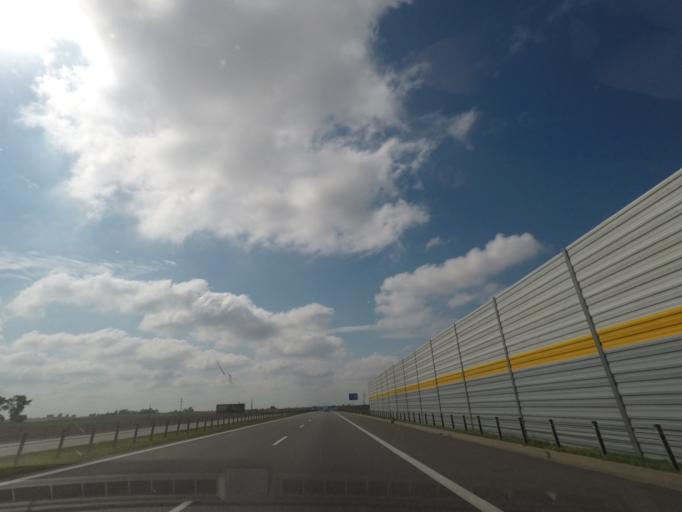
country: PL
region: Kujawsko-Pomorskie
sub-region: Powiat chelminski
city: Lisewo
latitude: 53.3031
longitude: 18.7065
